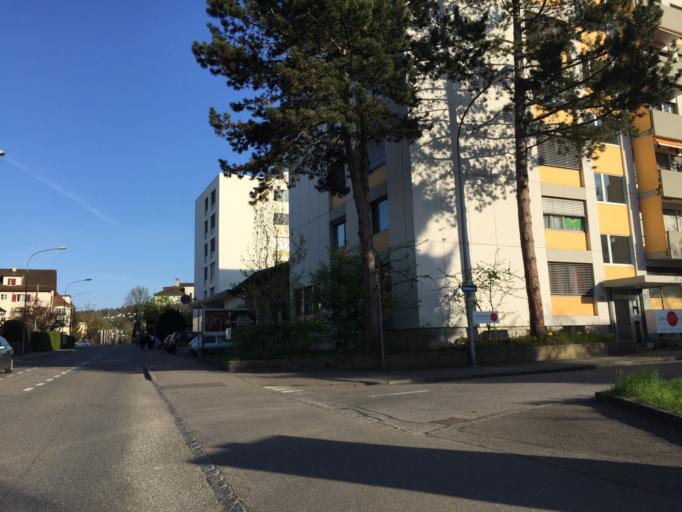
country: CH
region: Bern
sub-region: Bern-Mittelland District
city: Koniz
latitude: 46.9331
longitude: 7.4205
